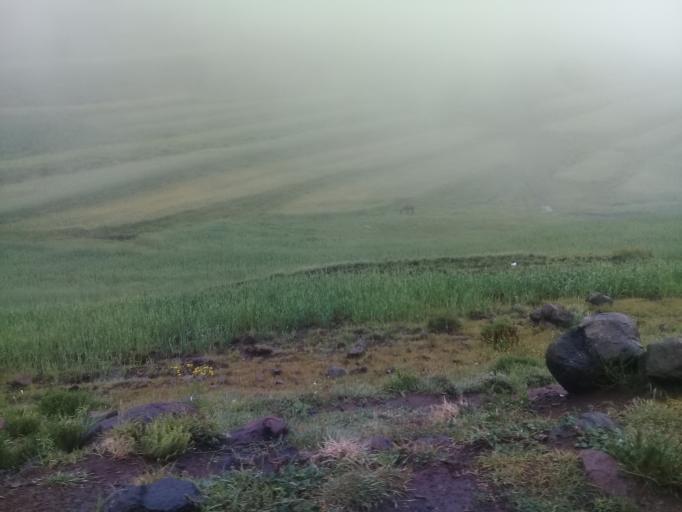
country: LS
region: Mokhotlong
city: Mokhotlong
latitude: -29.3878
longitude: 28.9746
